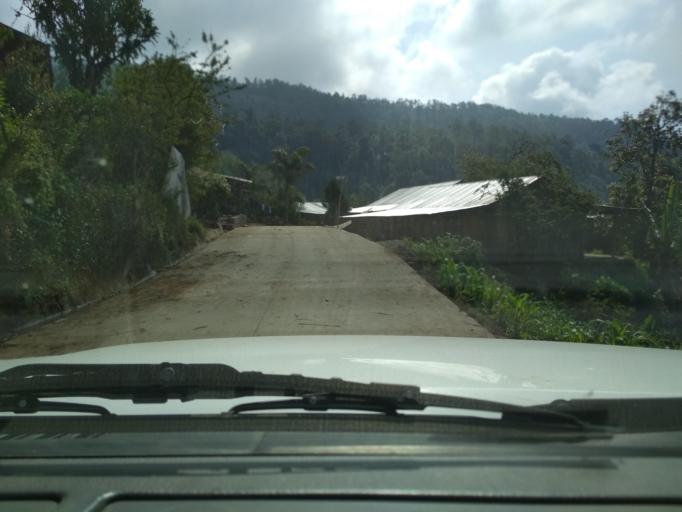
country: MX
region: Veracruz
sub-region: La Perla
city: Chilapa
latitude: 18.9941
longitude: -97.1769
